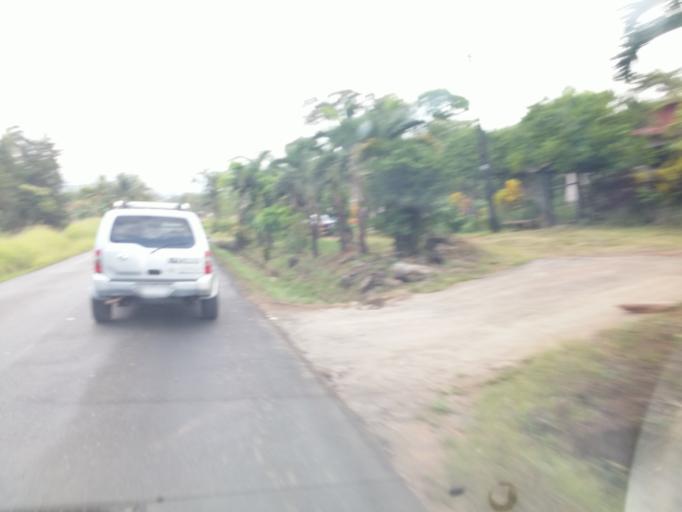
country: CR
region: Alajuela
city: Pital
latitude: 10.3939
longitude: -84.3383
